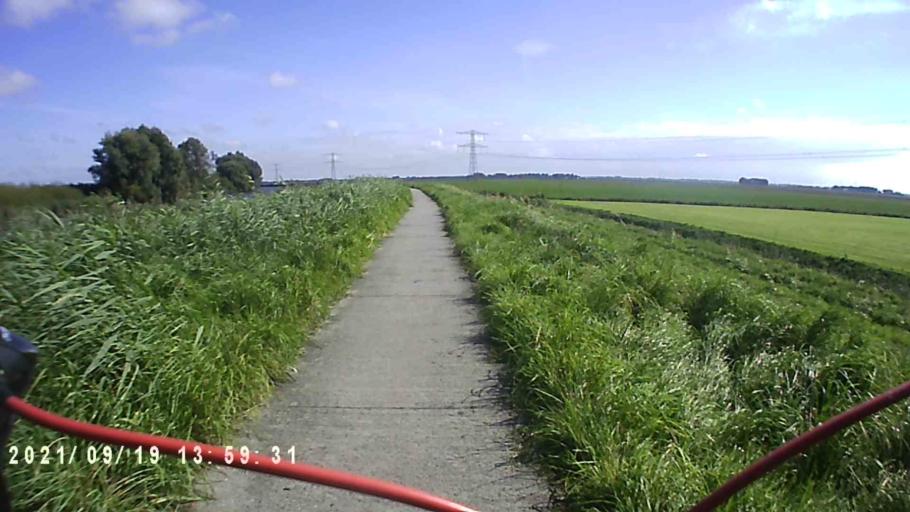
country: NL
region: Groningen
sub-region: Gemeente  Oldambt
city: Winschoten
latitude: 53.1429
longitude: 7.0987
